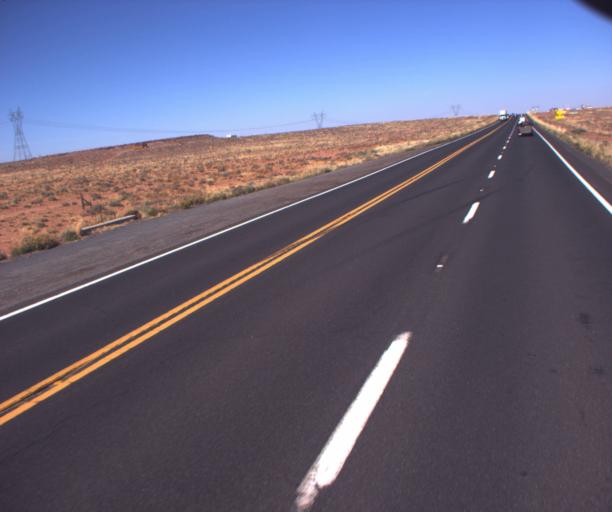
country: US
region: Arizona
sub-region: Coconino County
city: Tuba City
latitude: 35.8042
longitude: -111.4454
